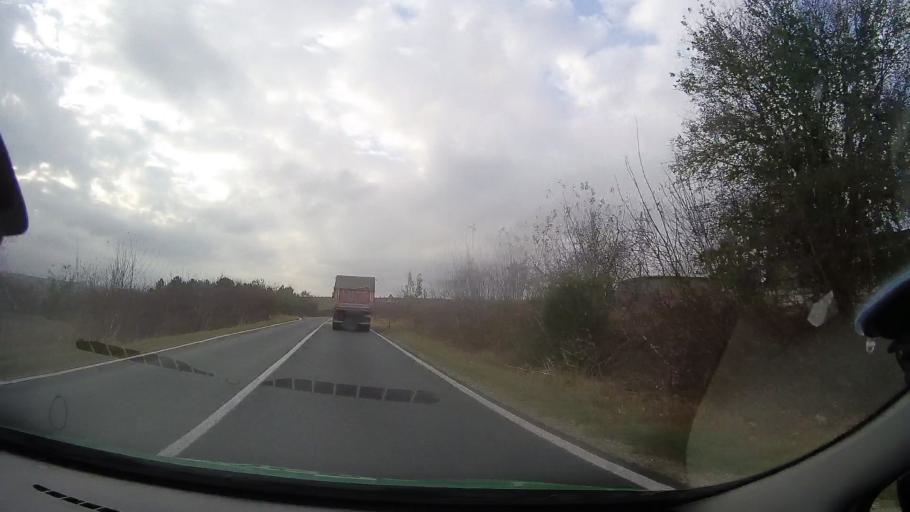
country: RO
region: Constanta
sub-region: Comuna Mircea Voda
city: Satu Nou
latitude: 44.2710
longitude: 28.1982
